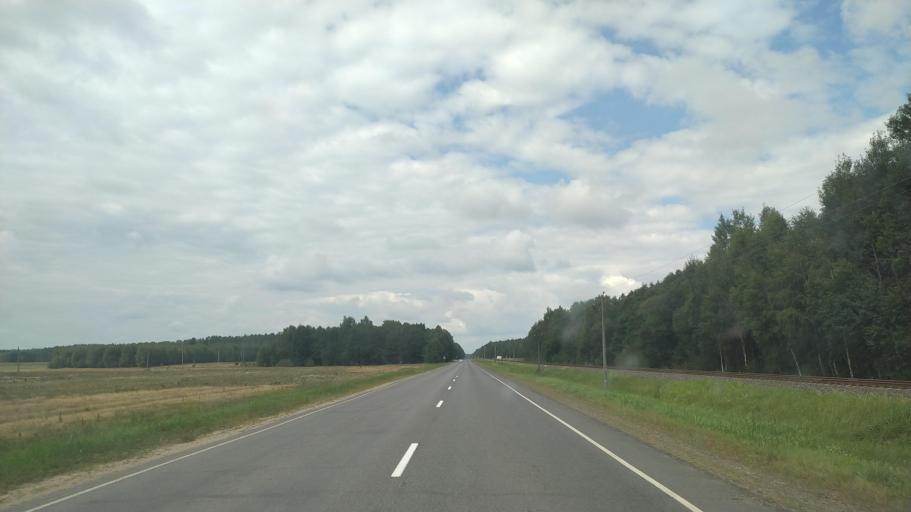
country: BY
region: Brest
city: Byelaazyorsk
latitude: 52.5377
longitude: 25.1397
